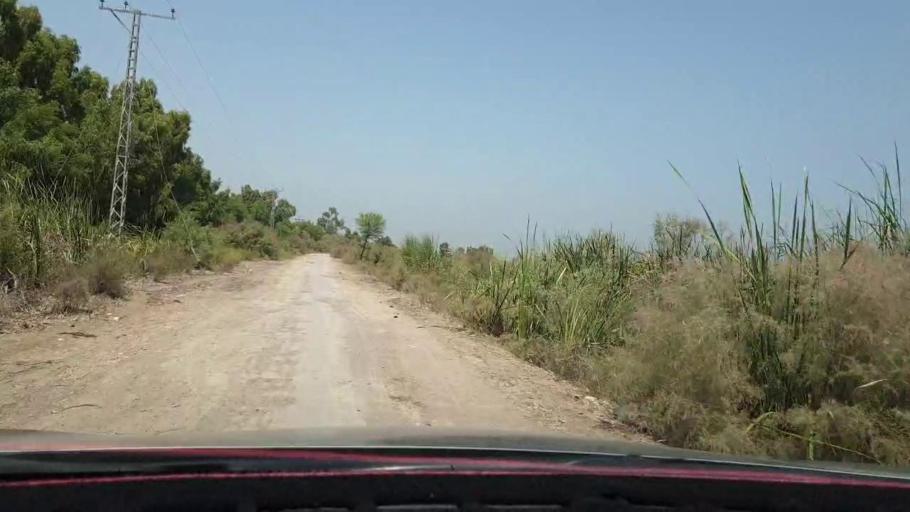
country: PK
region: Sindh
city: Warah
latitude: 27.4266
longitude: 67.6987
